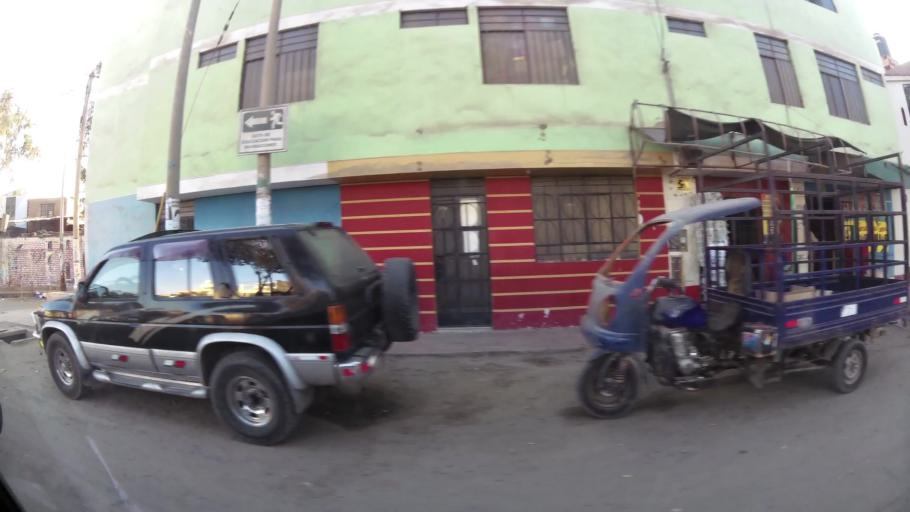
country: PE
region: Ica
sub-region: Provincia de Ica
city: Ica
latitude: -14.0596
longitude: -75.7338
